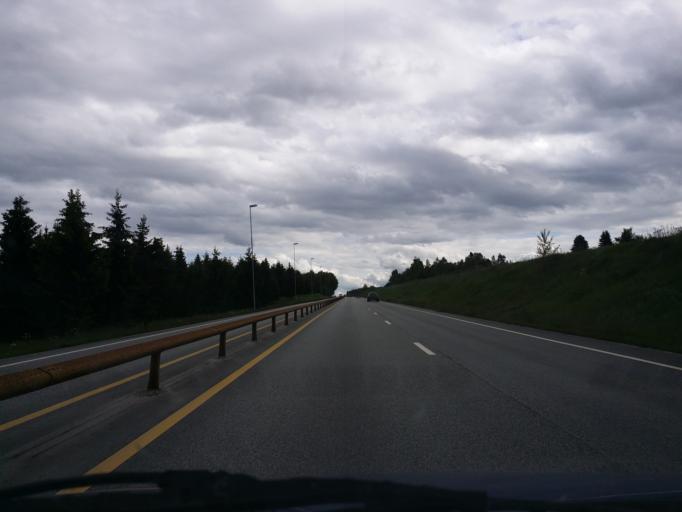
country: NO
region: Hedmark
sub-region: Stange
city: Stange
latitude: 60.7758
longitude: 11.1528
